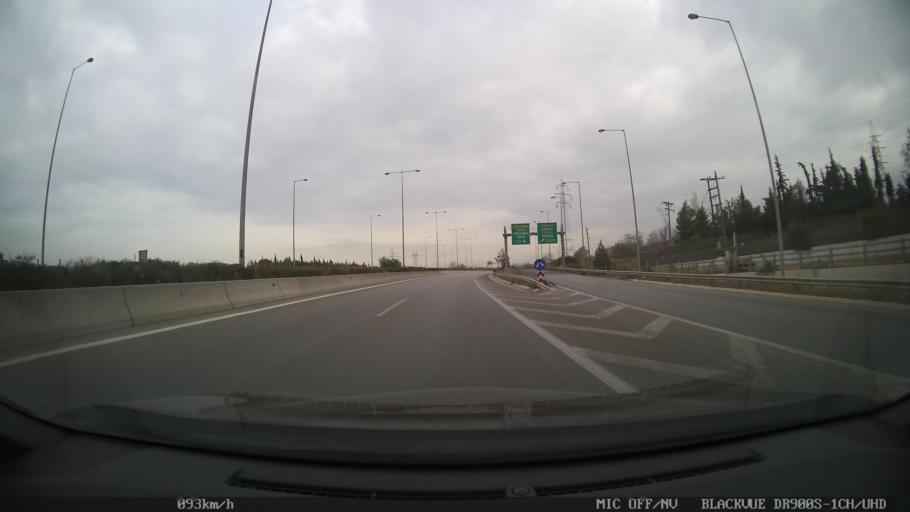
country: GR
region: Central Macedonia
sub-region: Nomos Thessalonikis
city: Efkarpia
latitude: 40.6956
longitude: 22.9541
